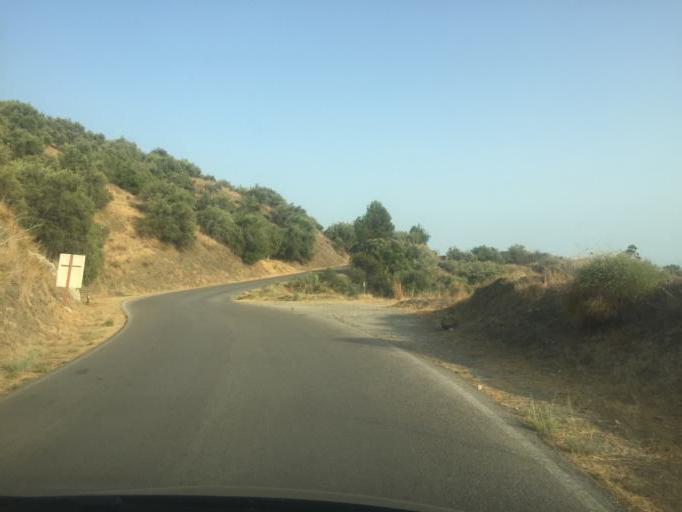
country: ES
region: Andalusia
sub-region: Provincia de Malaga
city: Frigiliana
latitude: 36.8024
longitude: -3.9125
